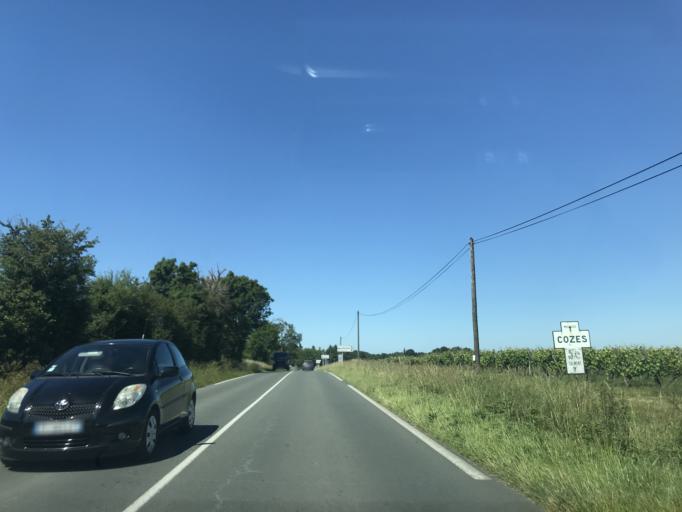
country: FR
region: Poitou-Charentes
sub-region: Departement de la Charente-Maritime
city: Cozes
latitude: 45.5792
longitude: -0.8198
